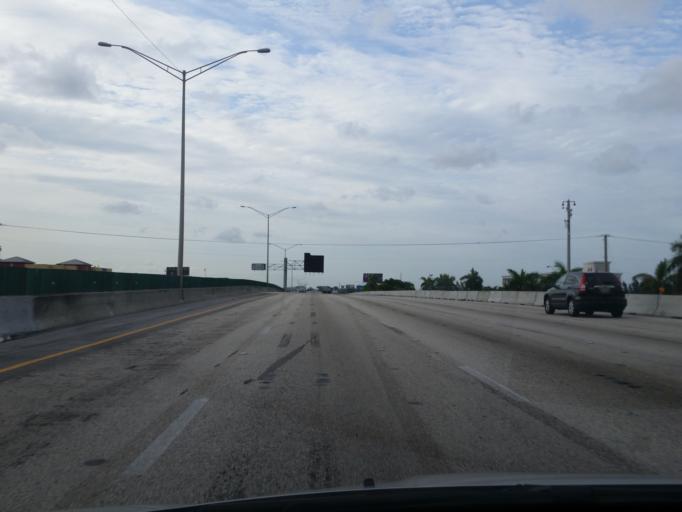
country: US
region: Florida
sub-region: Broward County
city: Pembroke Park
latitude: 25.9837
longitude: -80.1655
